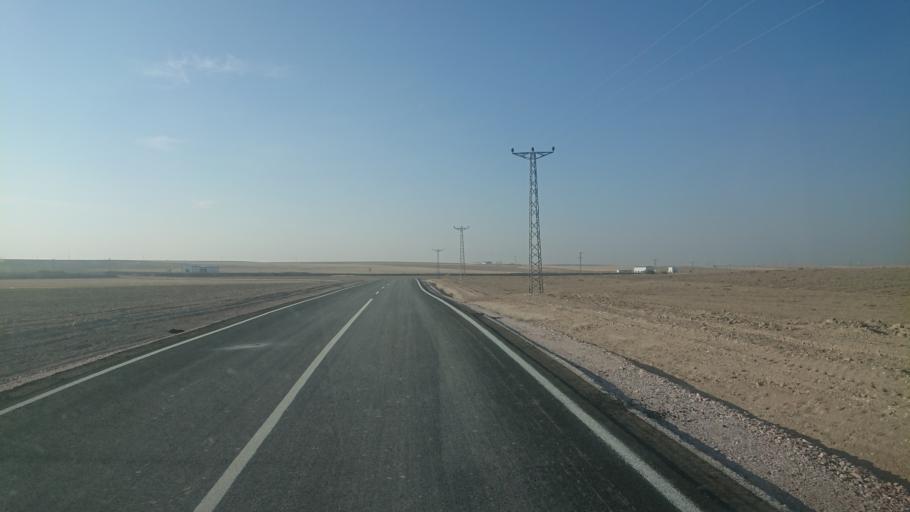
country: TR
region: Aksaray
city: Sultanhani
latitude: 38.0892
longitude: 33.6132
